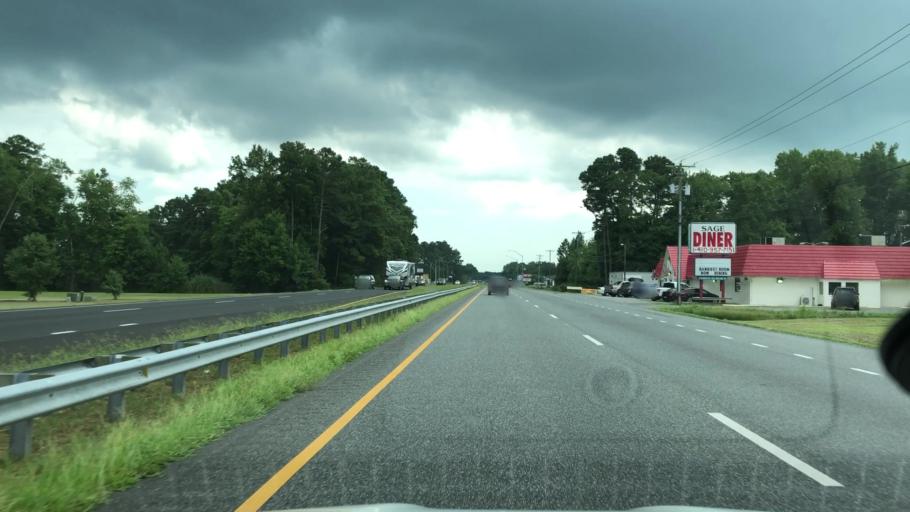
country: US
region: Maryland
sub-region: Worcester County
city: Pocomoke City
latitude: 38.0436
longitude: -75.5428
